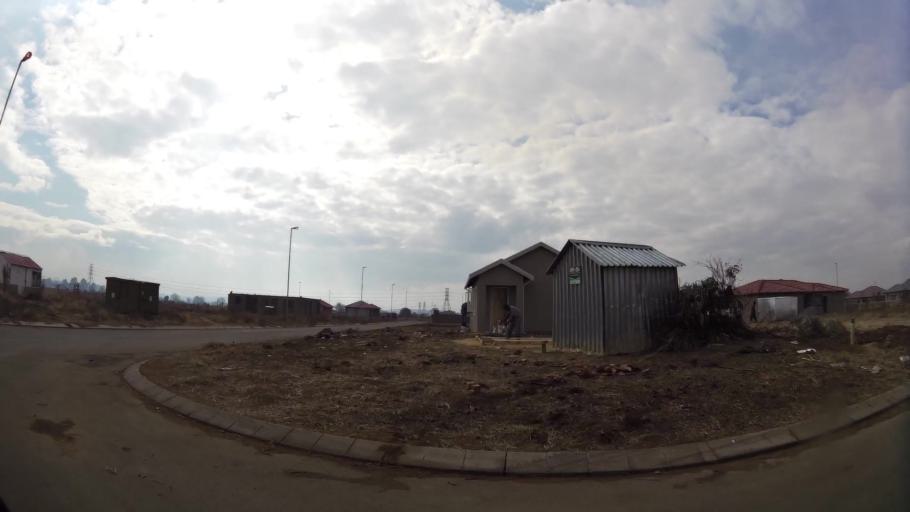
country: ZA
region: Gauteng
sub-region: Sedibeng District Municipality
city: Vanderbijlpark
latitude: -26.6802
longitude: 27.8426
